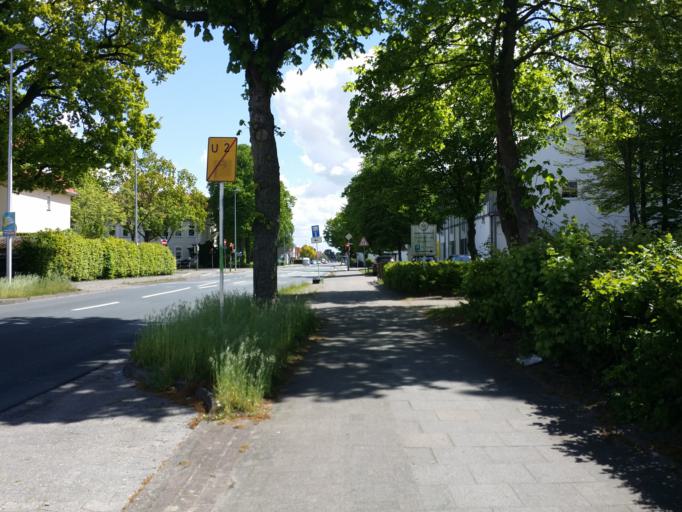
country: DE
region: Lower Saxony
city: Delmenhorst
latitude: 53.0299
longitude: 8.6272
